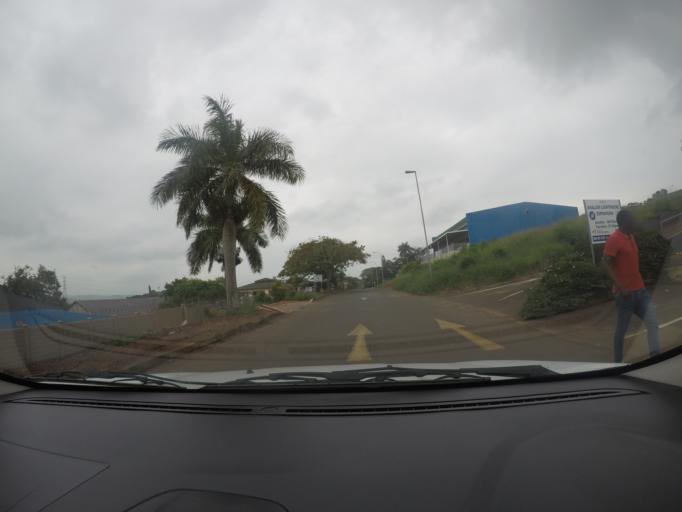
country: ZA
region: KwaZulu-Natal
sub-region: uThungulu District Municipality
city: Empangeni
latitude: -28.7386
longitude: 31.8929
